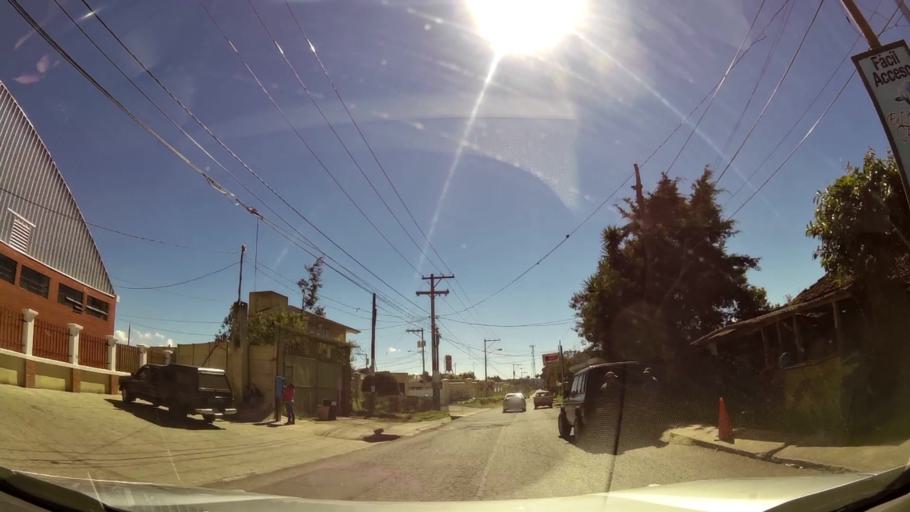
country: GT
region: Guatemala
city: San Jose Pinula
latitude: 14.5134
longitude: -90.4262
